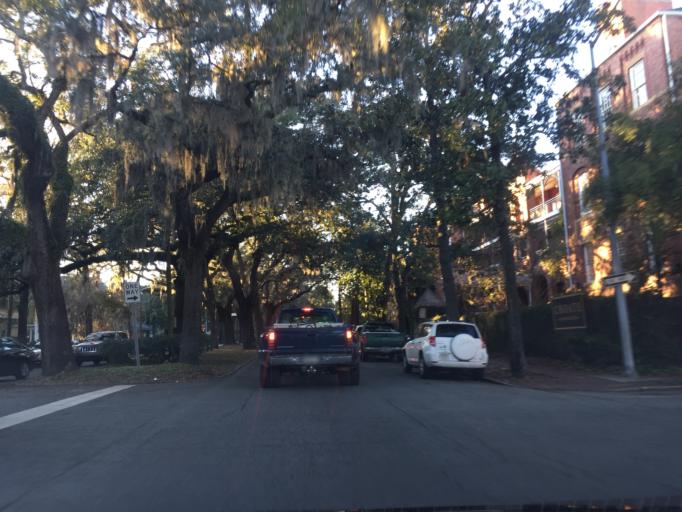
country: US
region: Georgia
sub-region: Chatham County
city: Savannah
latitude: 32.0563
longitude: -81.0966
